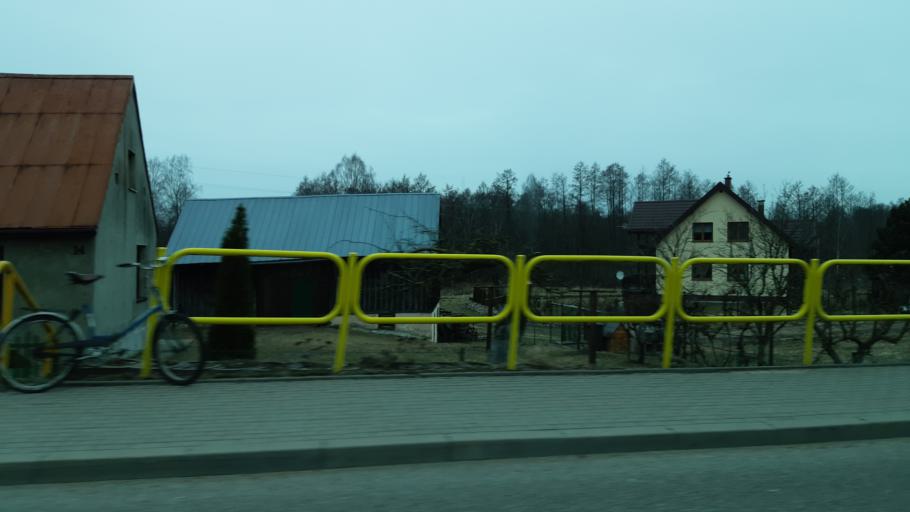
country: PL
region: Podlasie
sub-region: Suwalki
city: Suwalki
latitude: 54.3204
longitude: 22.9669
